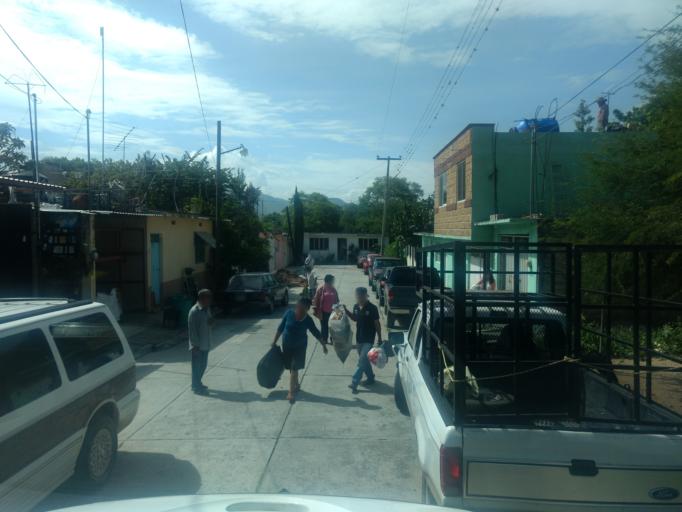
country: MX
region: Oaxaca
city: Ciudad de Huajuapam de Leon
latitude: 17.7992
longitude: -97.7859
